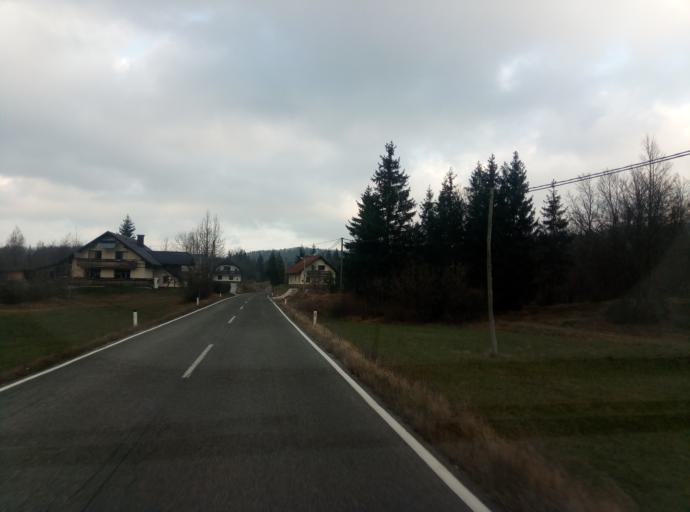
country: SI
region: Idrija
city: Idrija
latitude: 45.9322
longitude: 14.0656
